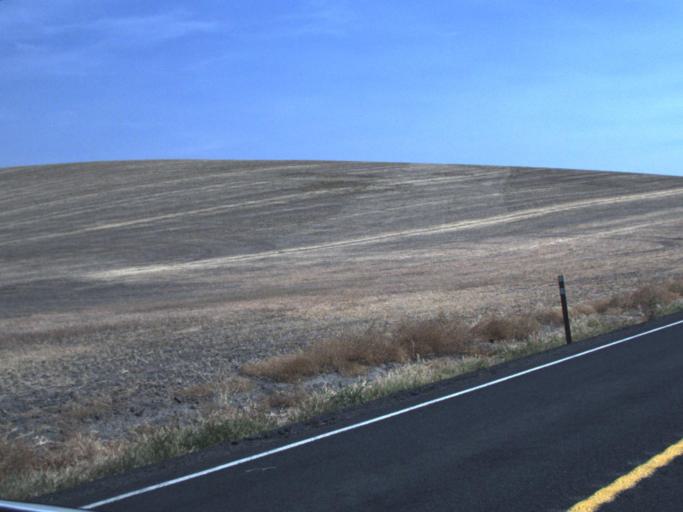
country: US
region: Idaho
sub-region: Benewah County
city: Plummer
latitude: 47.1949
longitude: -117.1223
